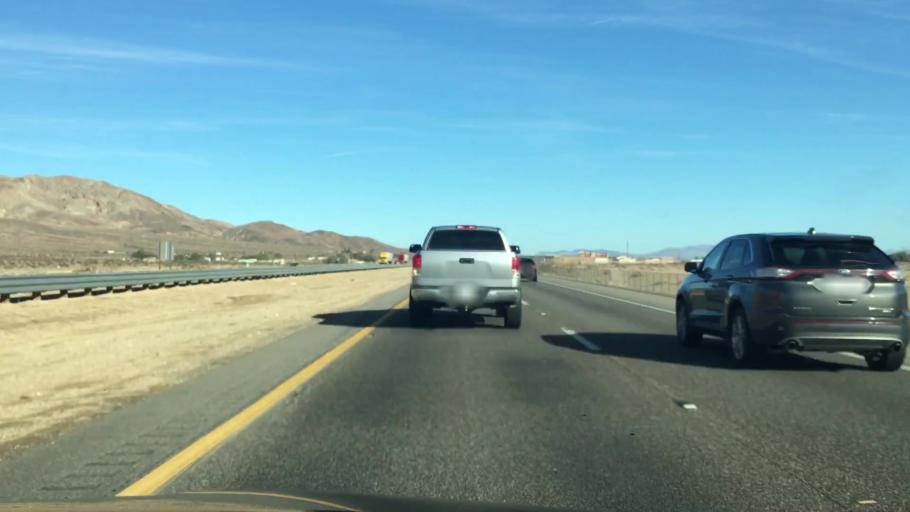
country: US
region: California
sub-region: San Bernardino County
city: Barstow
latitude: 34.9104
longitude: -116.8292
